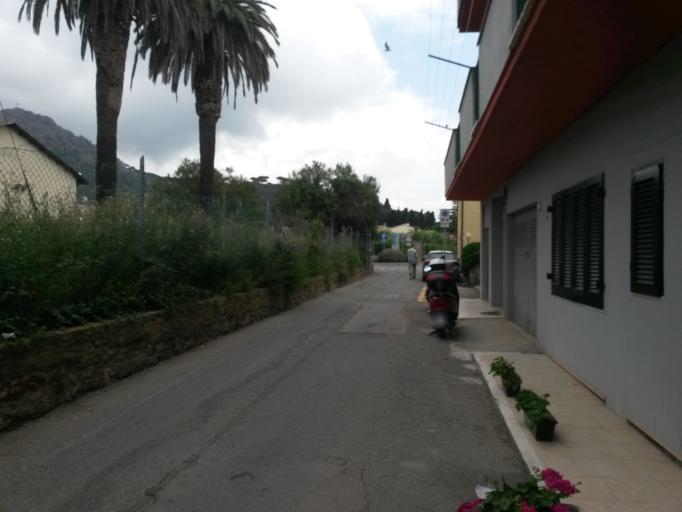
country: IT
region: Tuscany
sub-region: Provincia di Livorno
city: Porto Azzurro
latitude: 42.7671
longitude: 10.3941
